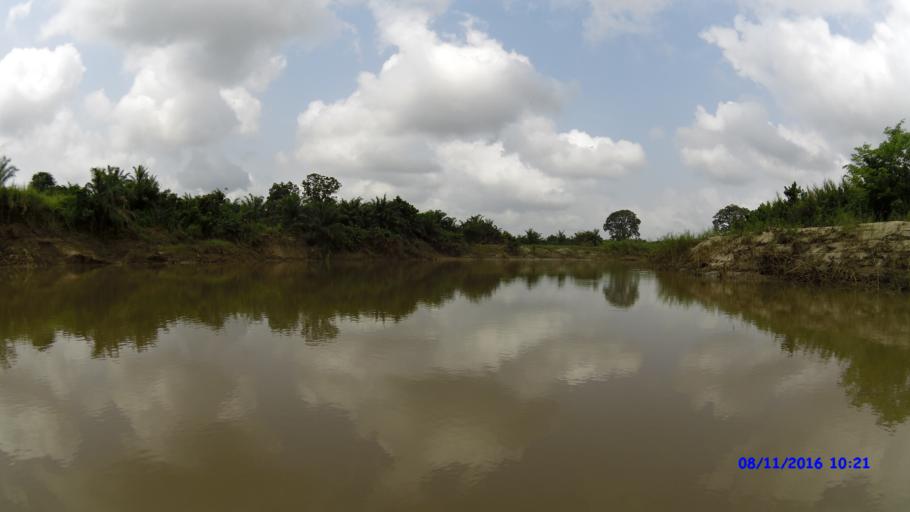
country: BJ
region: Mono
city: Come
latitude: 6.4621
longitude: 1.7465
